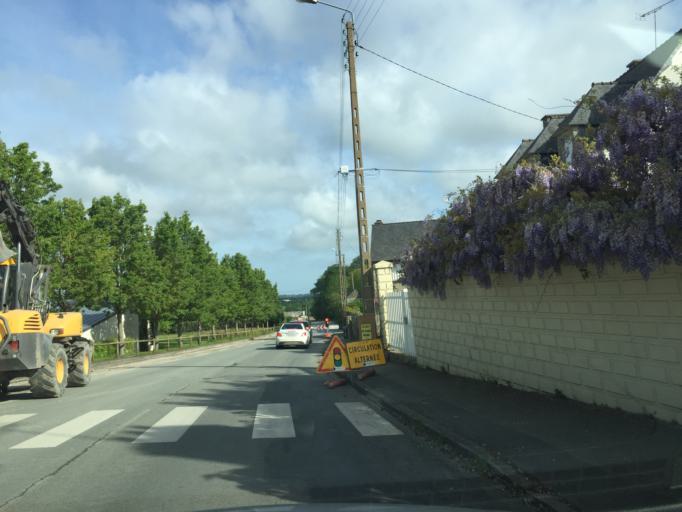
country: FR
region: Brittany
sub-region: Departement des Cotes-d'Armor
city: Matignon
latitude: 48.5981
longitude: -2.2936
